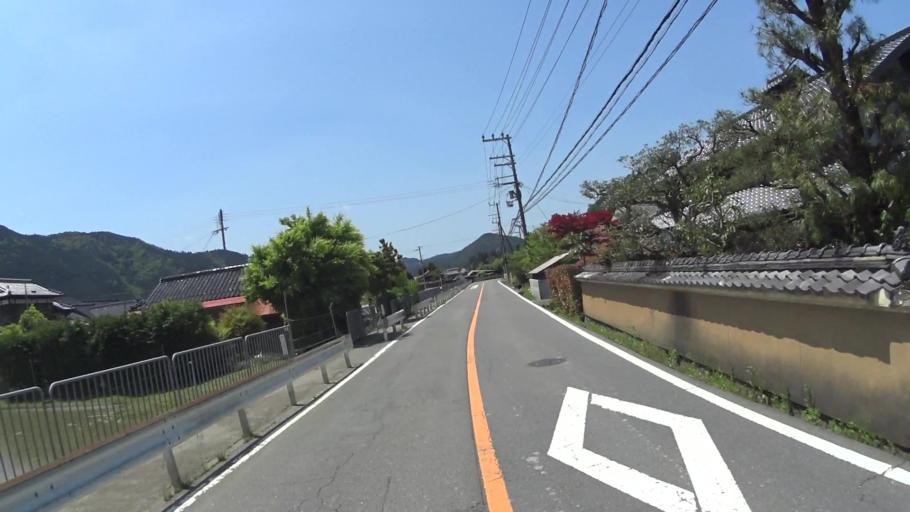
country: JP
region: Kyoto
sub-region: Kyoto-shi
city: Kamigyo-ku
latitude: 35.1833
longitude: 135.6679
